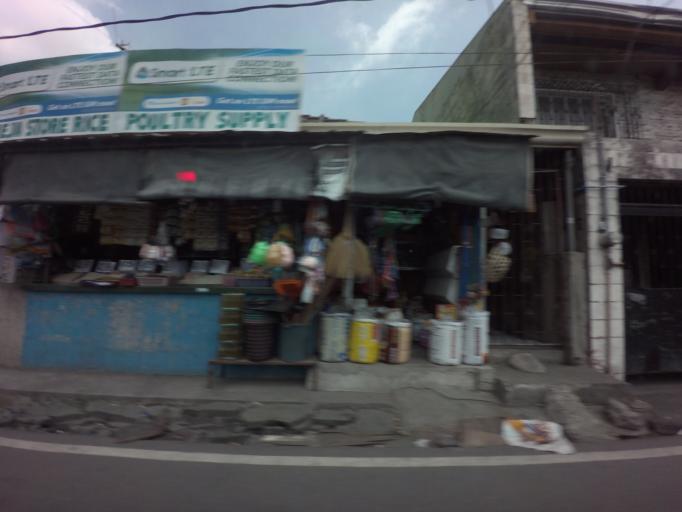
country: PH
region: Calabarzon
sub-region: Province of Rizal
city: Taguig
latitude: 14.4691
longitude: 121.0571
